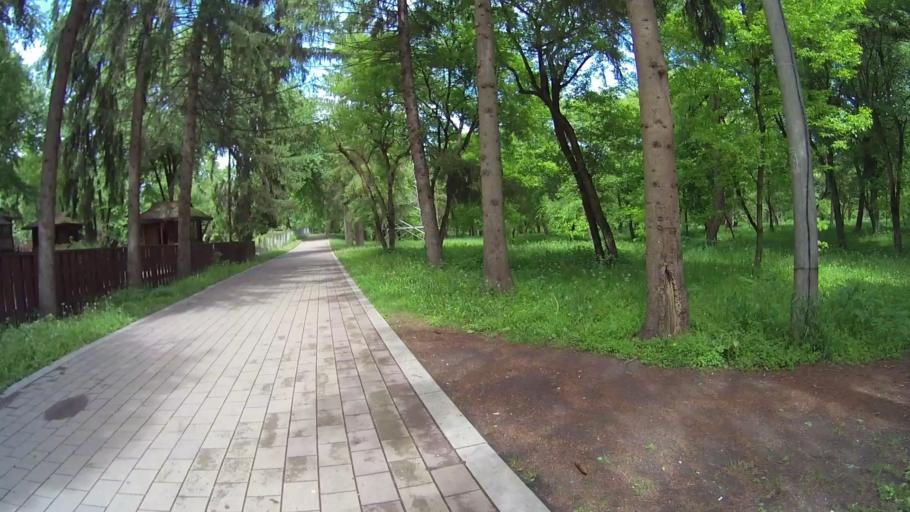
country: RU
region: Kabardino-Balkariya
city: Vol'nyy Aul
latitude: 43.4605
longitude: 43.5874
